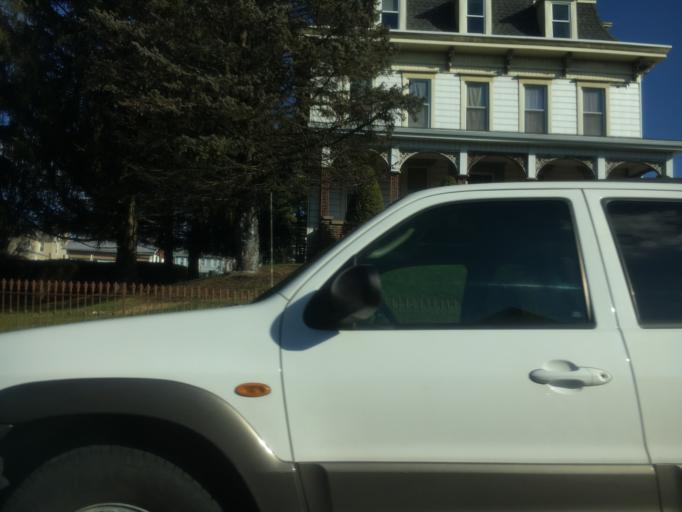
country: US
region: Pennsylvania
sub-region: Lehigh County
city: Coplay
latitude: 40.6757
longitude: -75.4864
